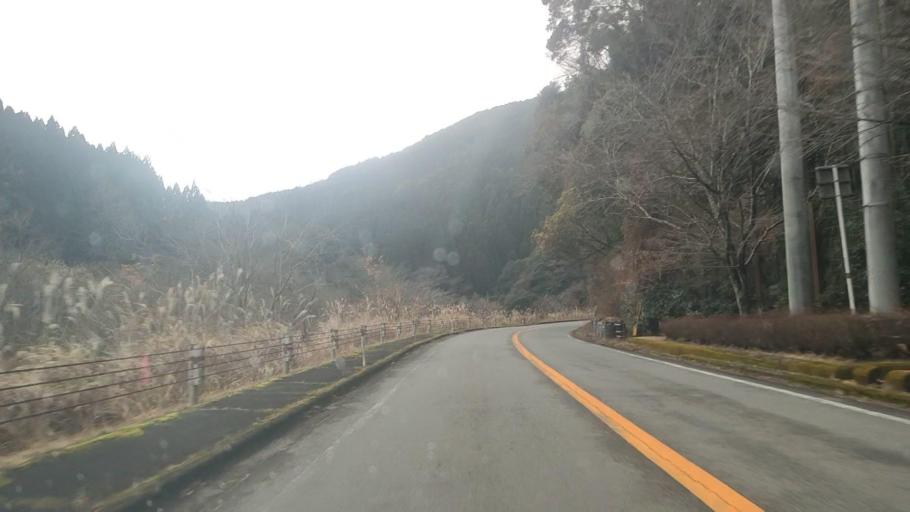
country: JP
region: Kumamoto
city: Hitoyoshi
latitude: 32.1223
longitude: 130.8100
